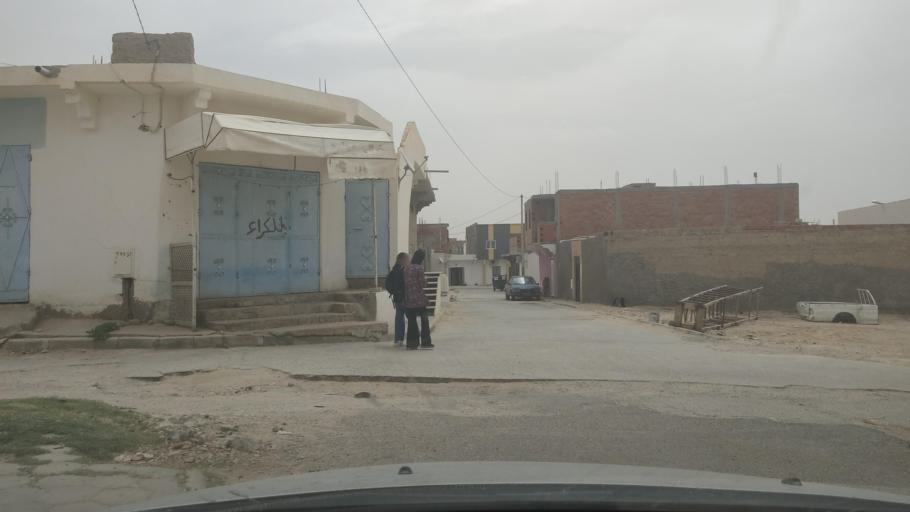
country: TN
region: Gafsa
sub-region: Gafsa Municipality
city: Gafsa
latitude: 34.3350
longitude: 8.9521
